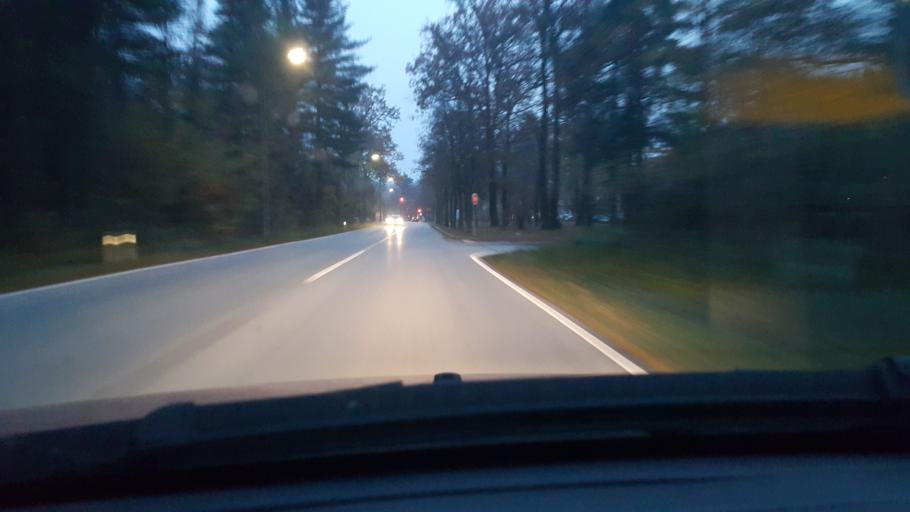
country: SI
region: Kidricevo
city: Kidricevo
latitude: 46.4066
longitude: 15.7993
